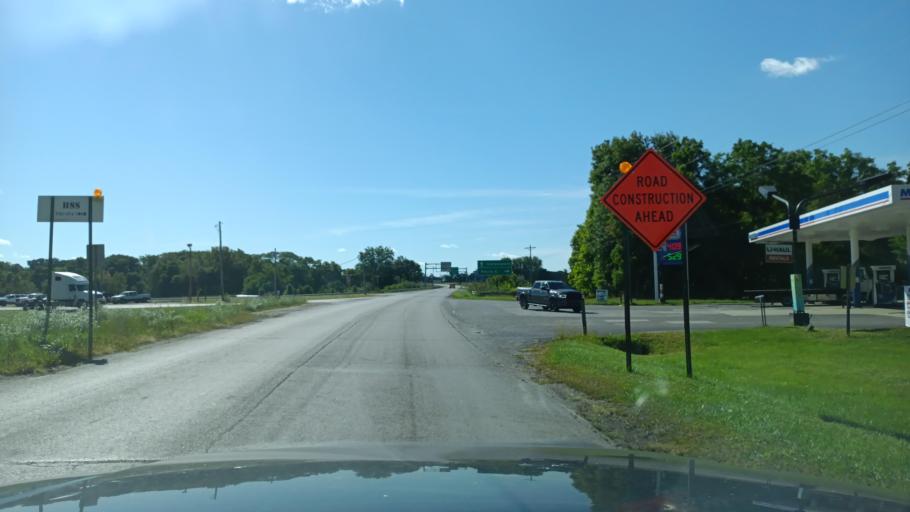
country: US
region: Indiana
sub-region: Fountain County
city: Covington
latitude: 40.1242
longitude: -87.3818
